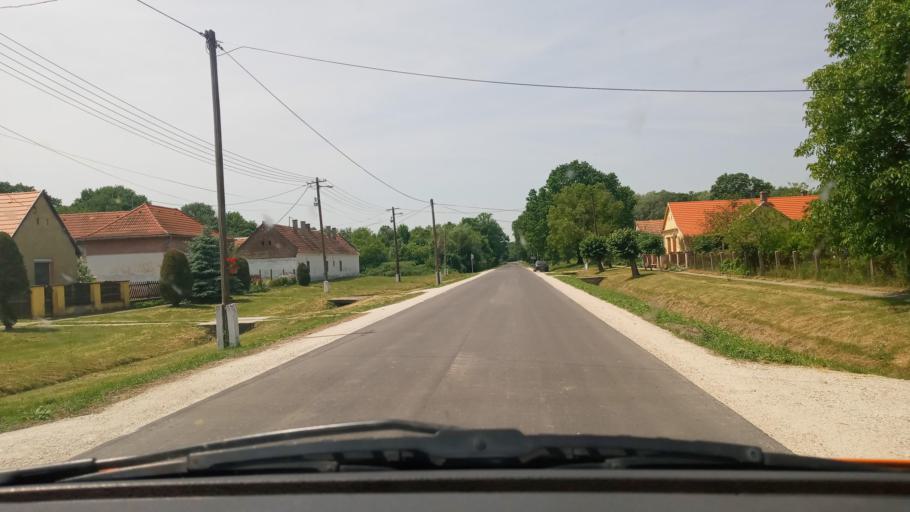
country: HU
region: Baranya
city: Szigetvar
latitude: 45.9589
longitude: 17.6550
